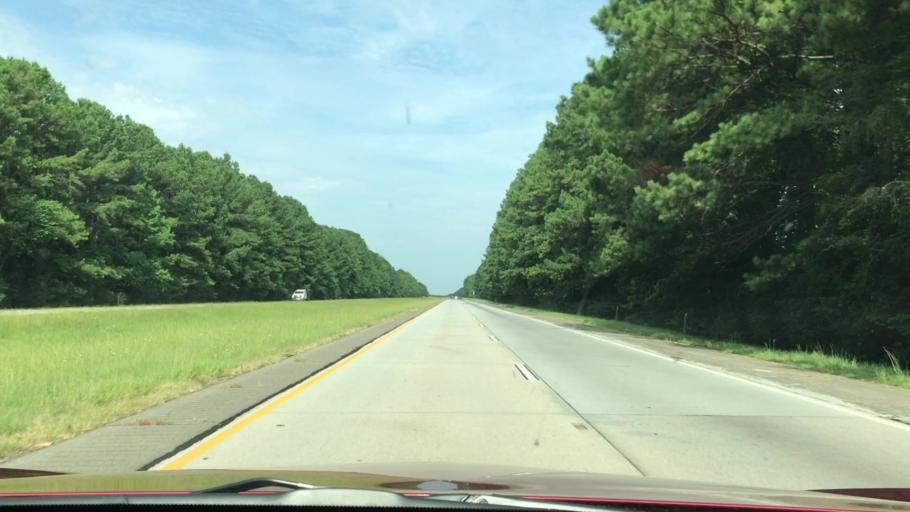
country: US
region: Georgia
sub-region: Warren County
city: Firing Range
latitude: 33.5040
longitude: -82.7367
